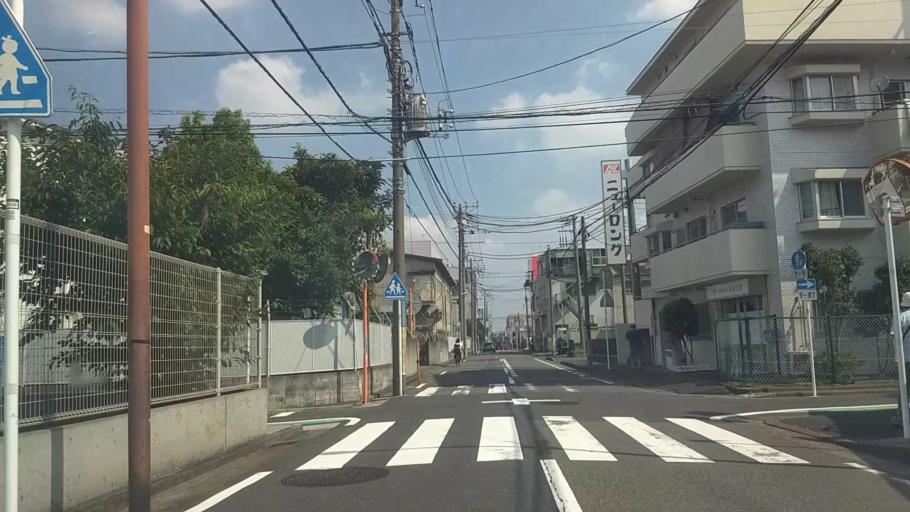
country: JP
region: Kanagawa
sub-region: Kawasaki-shi
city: Kawasaki
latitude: 35.5231
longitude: 139.6822
